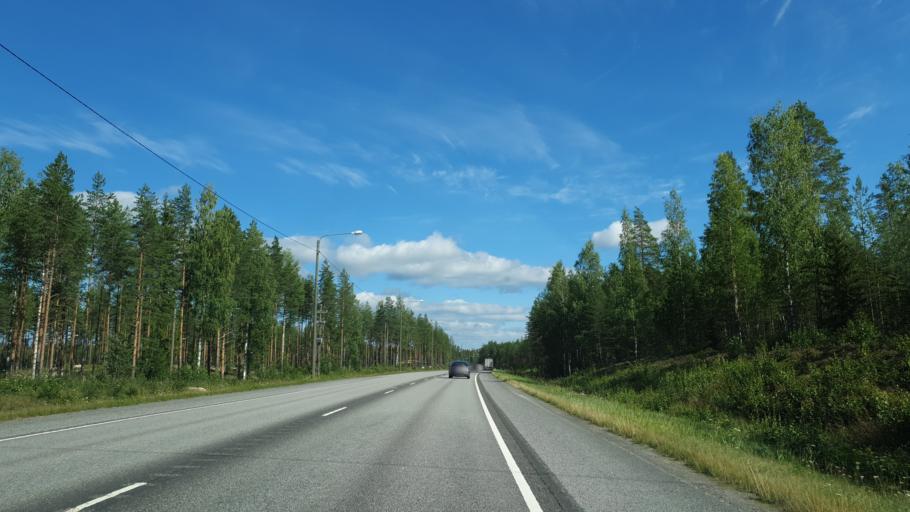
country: FI
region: Central Finland
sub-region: Jyvaeskylae
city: Toivakka
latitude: 62.2524
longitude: 26.1075
